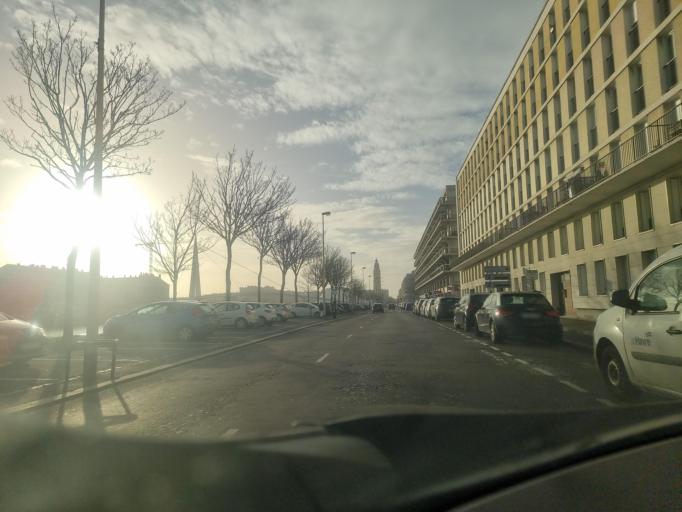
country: FR
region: Haute-Normandie
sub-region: Departement de la Seine-Maritime
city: Le Havre
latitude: 49.4908
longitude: 0.1154
